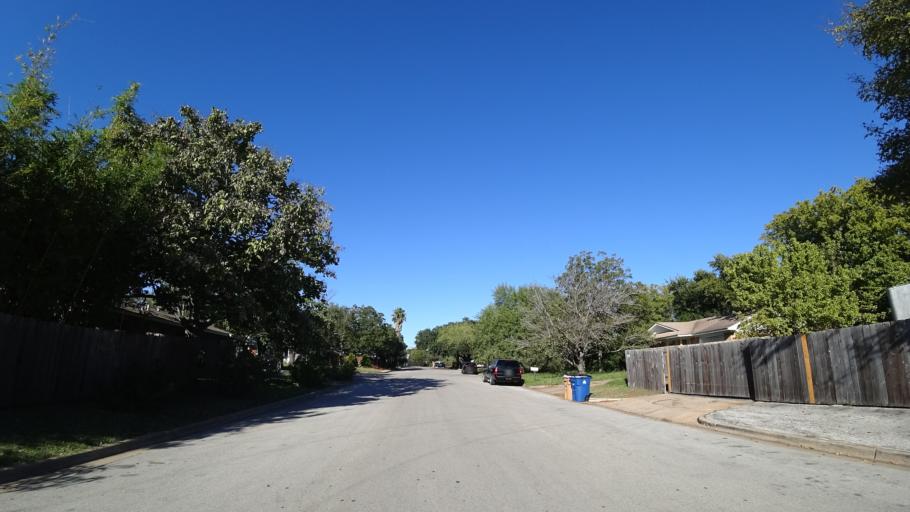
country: US
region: Texas
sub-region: Travis County
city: Rollingwood
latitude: 30.2337
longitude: -97.8083
